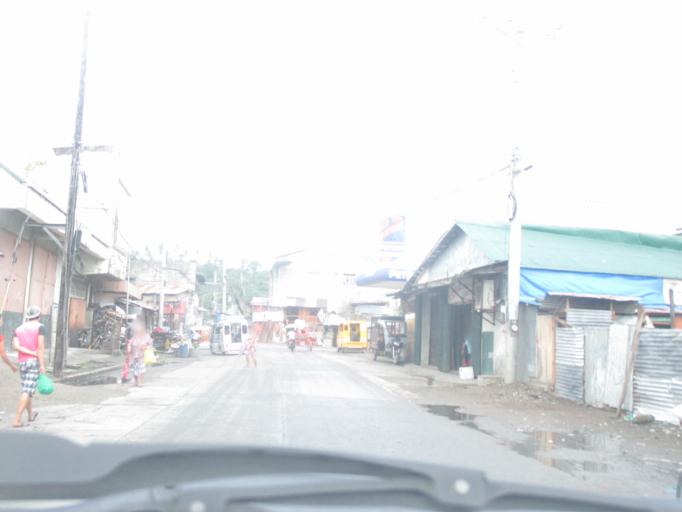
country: PH
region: Eastern Visayas
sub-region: Province of Leyte
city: Panalanoy
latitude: 11.2464
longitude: 124.9964
